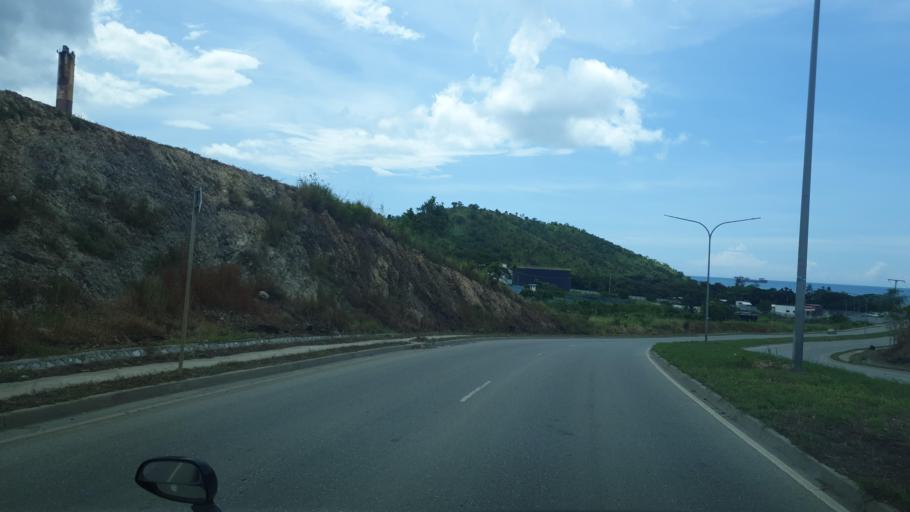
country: PG
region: National Capital
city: Port Moresby
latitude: -9.4302
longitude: 147.1413
